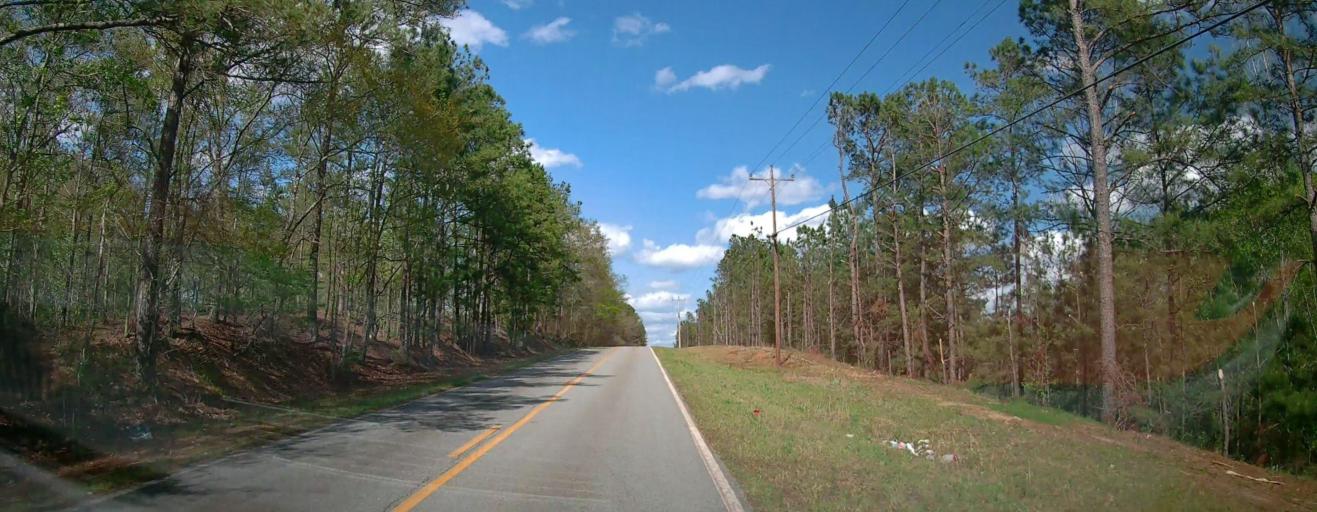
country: US
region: Georgia
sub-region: Wilkinson County
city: Gordon
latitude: 32.8091
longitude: -83.4096
